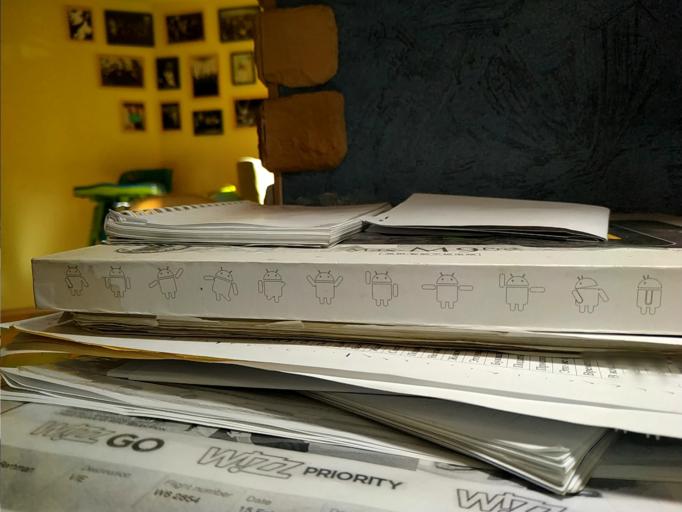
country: RU
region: Novgorod
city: Poddor'ye
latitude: 57.4760
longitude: 30.9793
